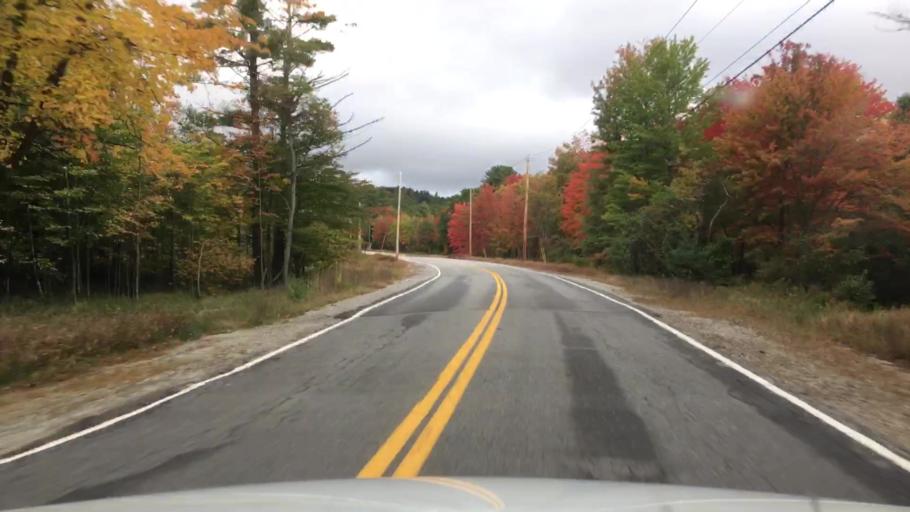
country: US
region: Maine
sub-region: Oxford County
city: Bethel
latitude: 44.3451
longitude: -70.7853
